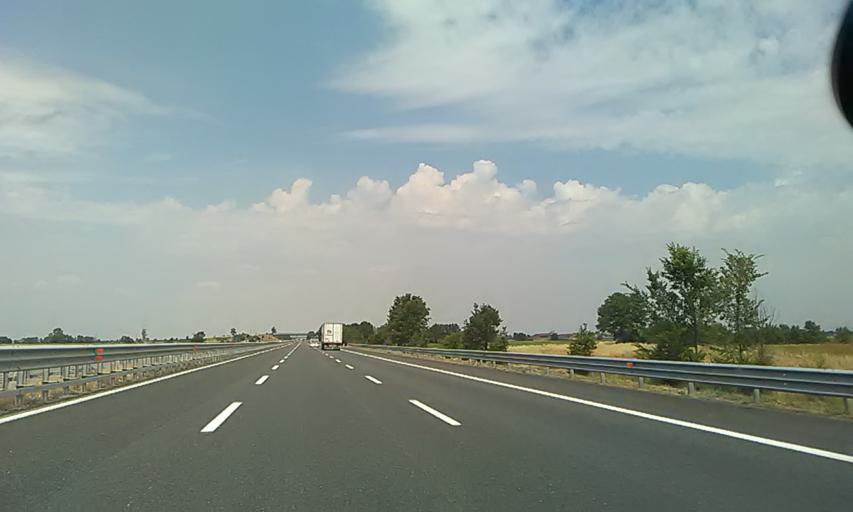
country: IT
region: Piedmont
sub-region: Provincia di Alessandria
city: Predosa
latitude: 44.7747
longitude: 8.6272
